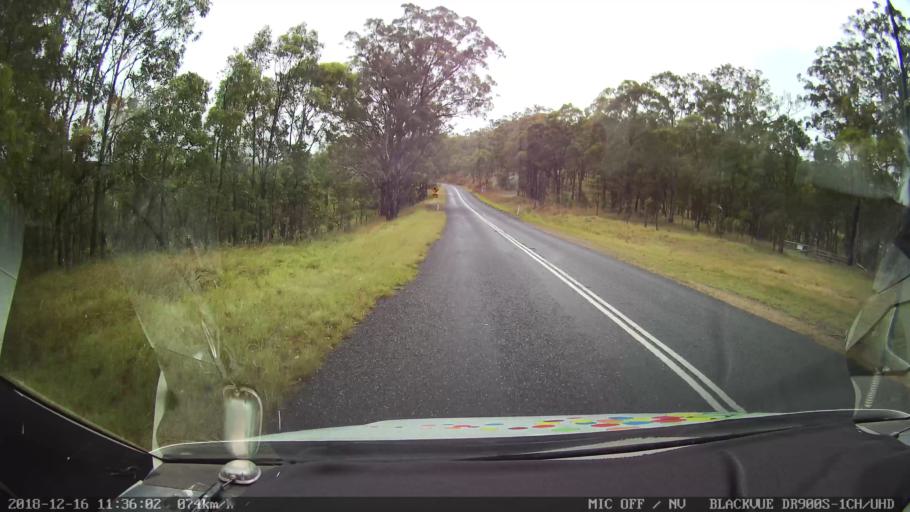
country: AU
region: New South Wales
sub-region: Tenterfield Municipality
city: Carrolls Creek
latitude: -28.9847
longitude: 152.1674
